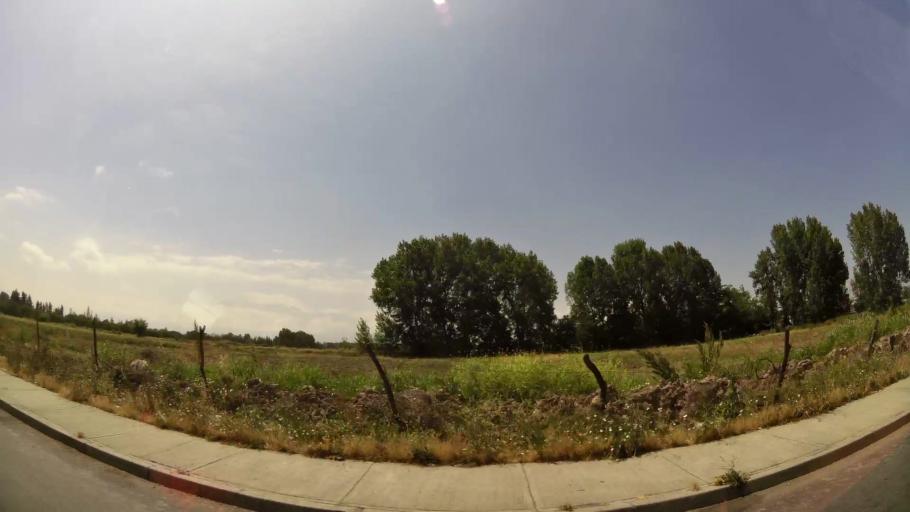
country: CL
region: Santiago Metropolitan
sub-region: Provincia de Santiago
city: Lo Prado
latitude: -33.5142
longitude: -70.7160
